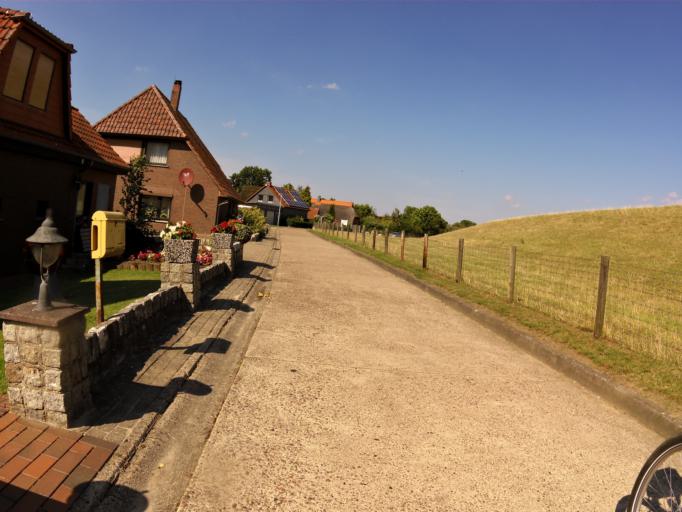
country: DE
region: Lower Saxony
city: Ovelgonne
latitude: 53.3929
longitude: 8.4592
